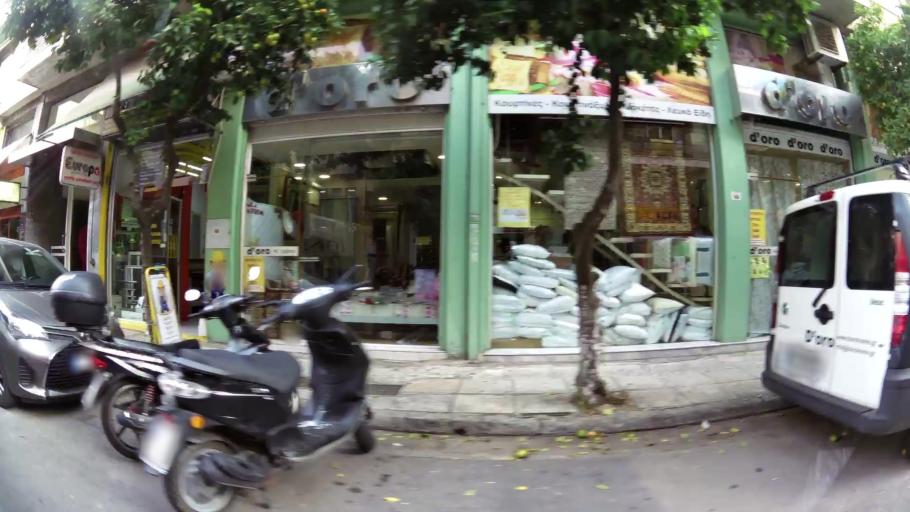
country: GR
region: Attica
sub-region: Nomarchia Athinas
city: Kipseli
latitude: 37.9907
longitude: 23.7481
